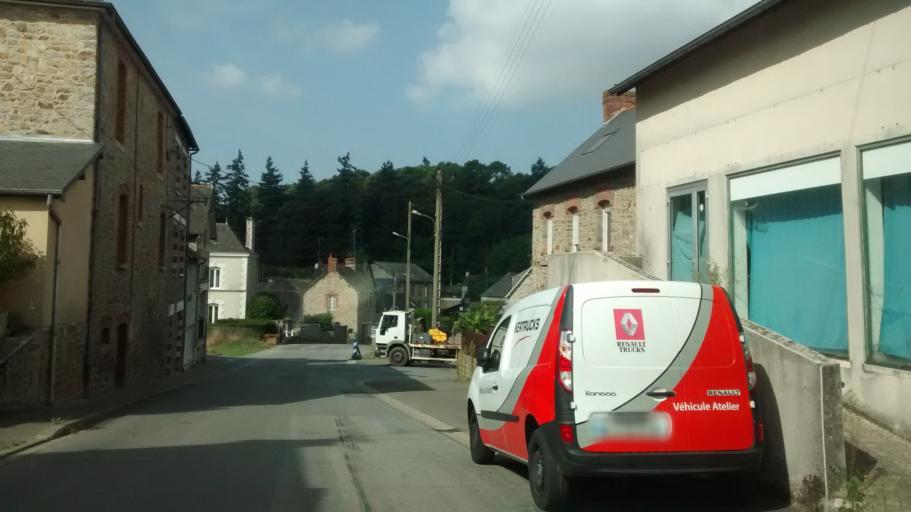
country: FR
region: Brittany
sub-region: Departement d'Ille-et-Vilaine
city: Chatillon-en-Vendelais
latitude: 48.2256
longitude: -1.1826
